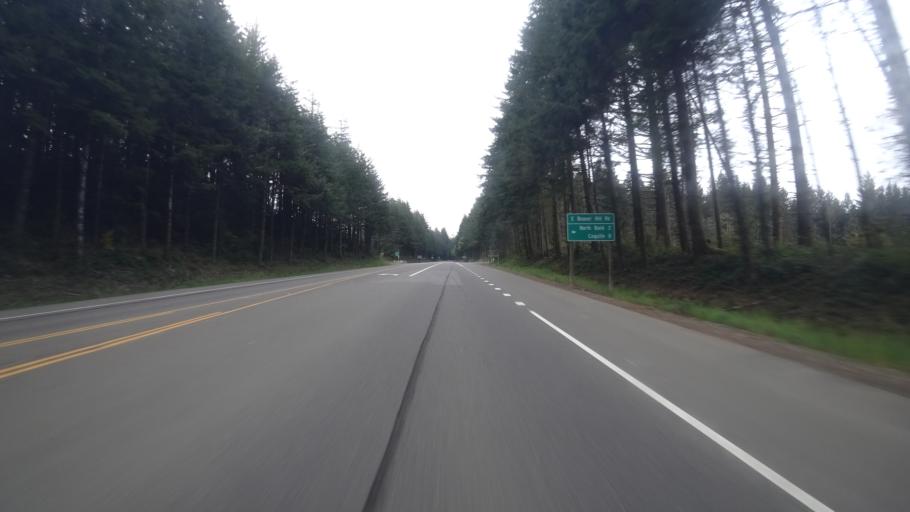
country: US
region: Oregon
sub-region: Coos County
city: Coquille
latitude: 43.2107
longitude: -124.3071
